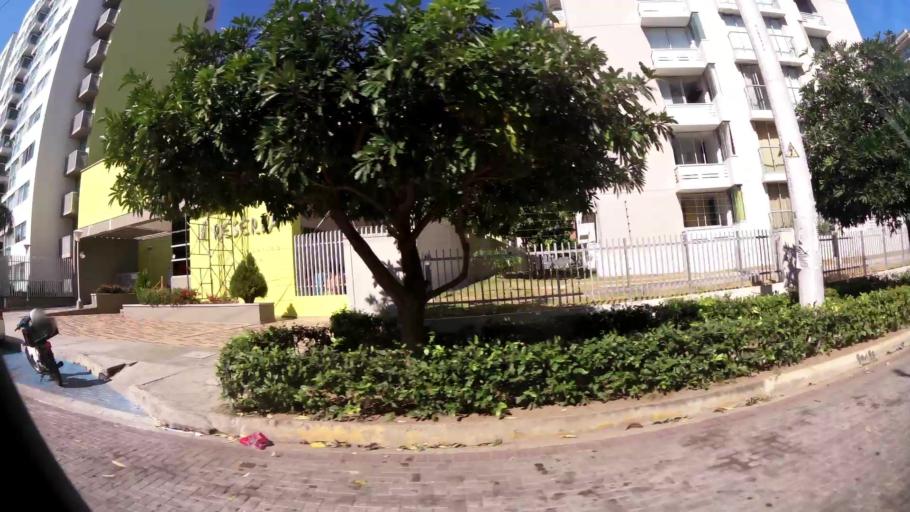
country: CO
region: Atlantico
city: Barranquilla
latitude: 11.0218
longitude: -74.8172
